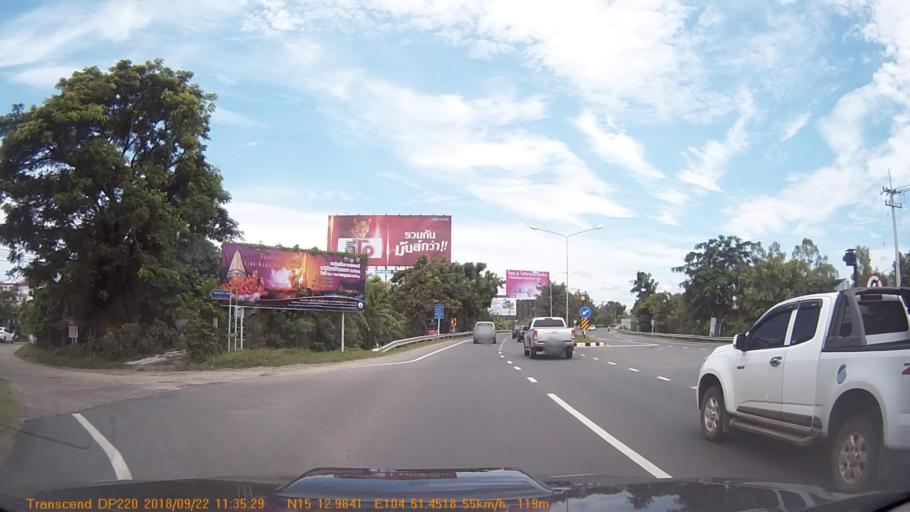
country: TH
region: Changwat Ubon Ratchathani
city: Warin Chamrap
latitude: 15.2164
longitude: 104.8575
